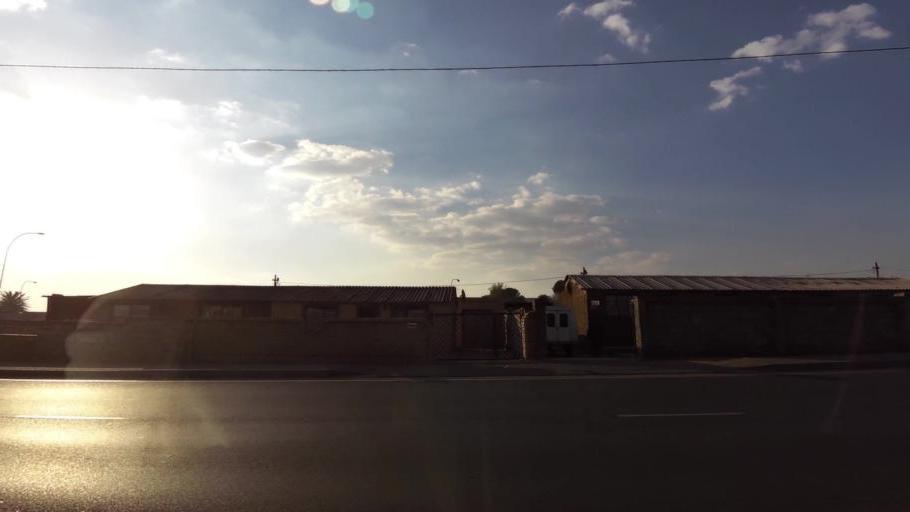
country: ZA
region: Gauteng
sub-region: City of Johannesburg Metropolitan Municipality
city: Roodepoort
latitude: -26.2125
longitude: 27.8928
